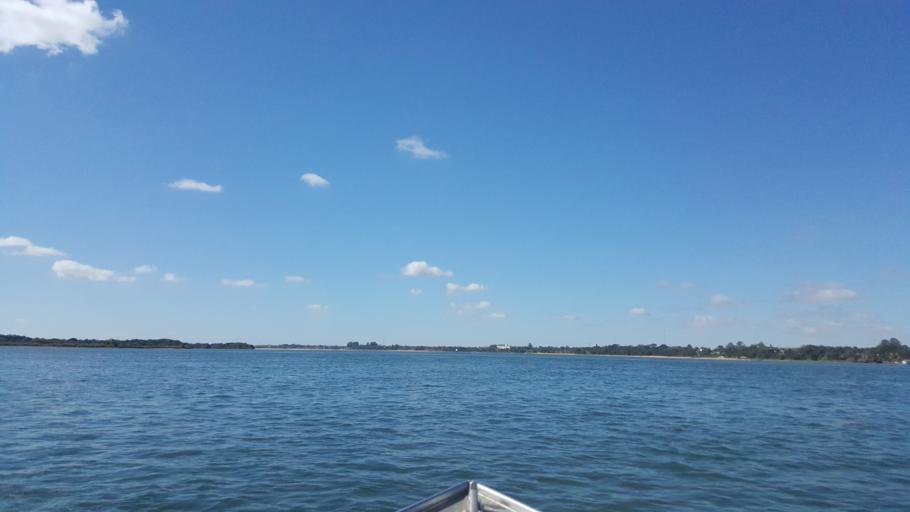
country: AR
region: Corrientes
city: Ituzaingo
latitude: -27.5833
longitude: -56.7060
